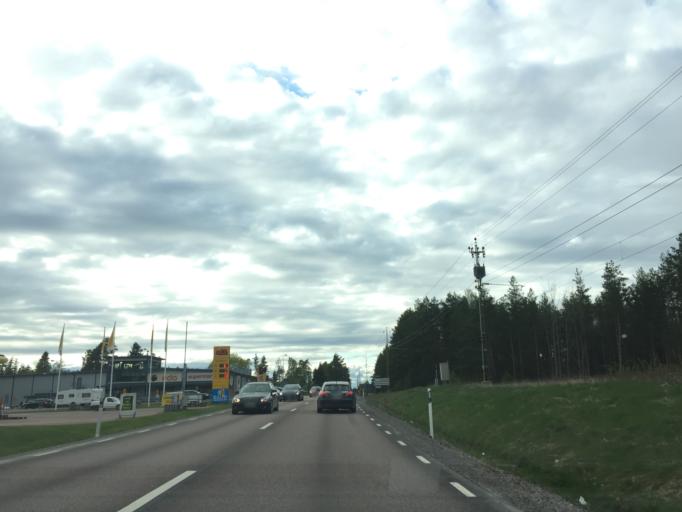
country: SE
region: Vaermland
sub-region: Eda Kommun
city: Charlottenberg
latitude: 59.9230
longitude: 12.2631
